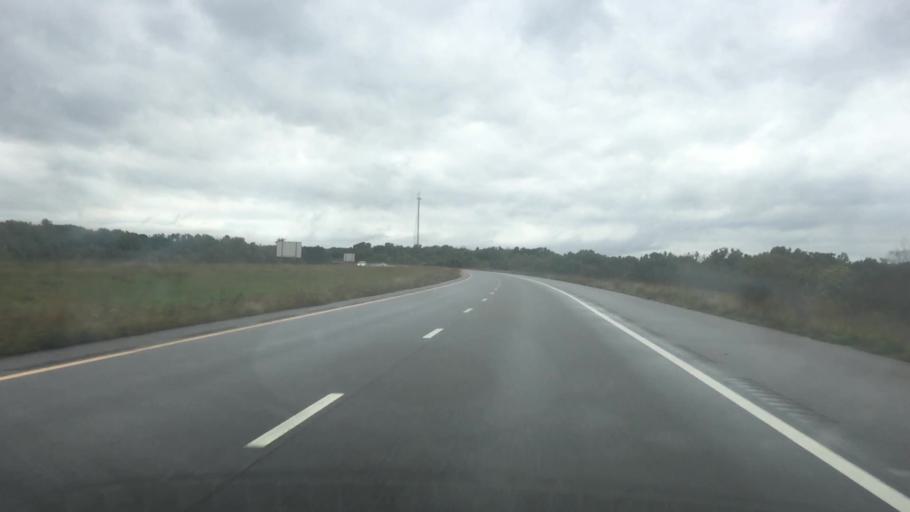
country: US
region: Kansas
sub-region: Miami County
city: Osawatomie
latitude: 38.4891
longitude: -94.9431
